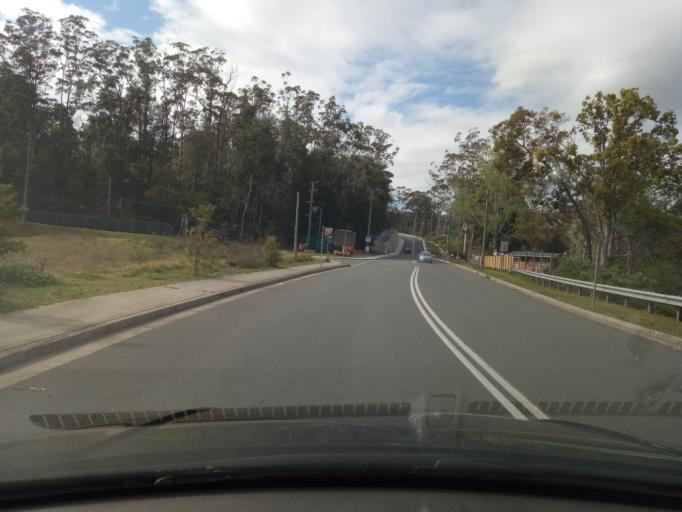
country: AU
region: New South Wales
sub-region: Gosford Shire
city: Lisarow
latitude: -33.3883
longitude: 151.3806
